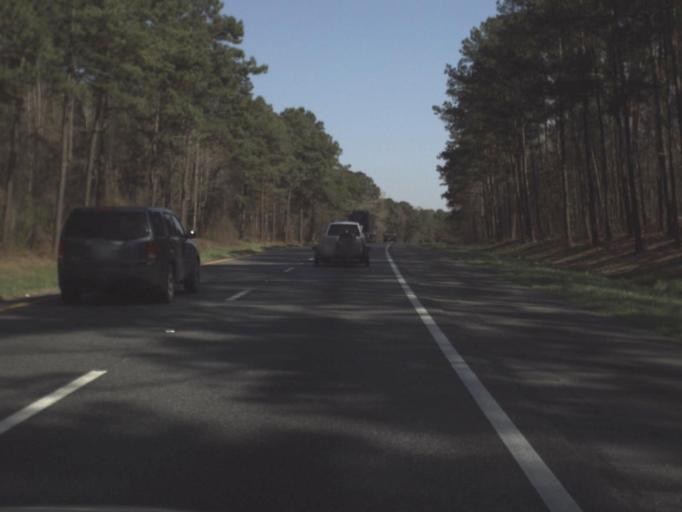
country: US
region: Florida
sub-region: Gadsden County
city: Midway
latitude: 30.5280
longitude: -84.5052
